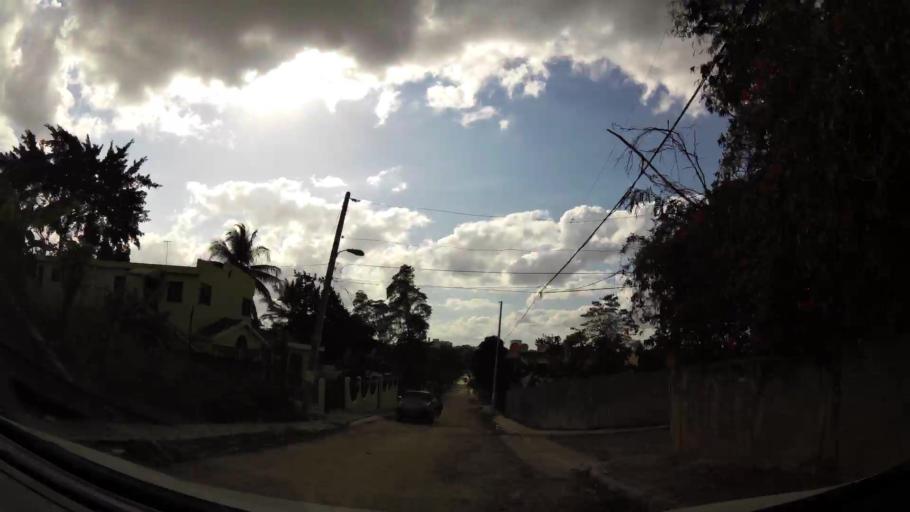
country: DO
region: Nacional
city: Ensanche Luperon
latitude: 18.5565
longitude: -69.8985
